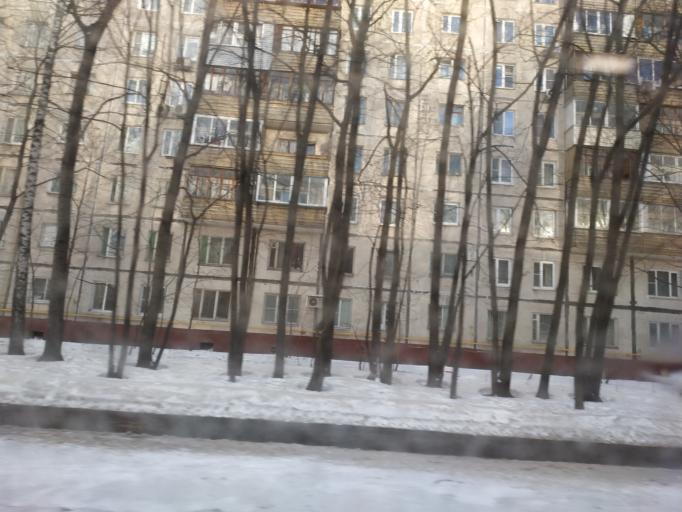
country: RU
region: Moskovskaya
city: Izmaylovo
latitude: 55.7998
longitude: 37.8191
